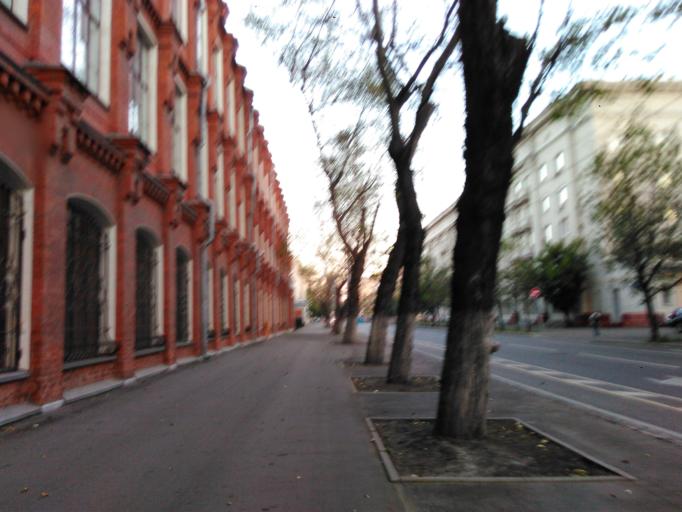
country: RU
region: Moscow
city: Zamoskvorech'ye
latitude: 55.7196
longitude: 37.6181
